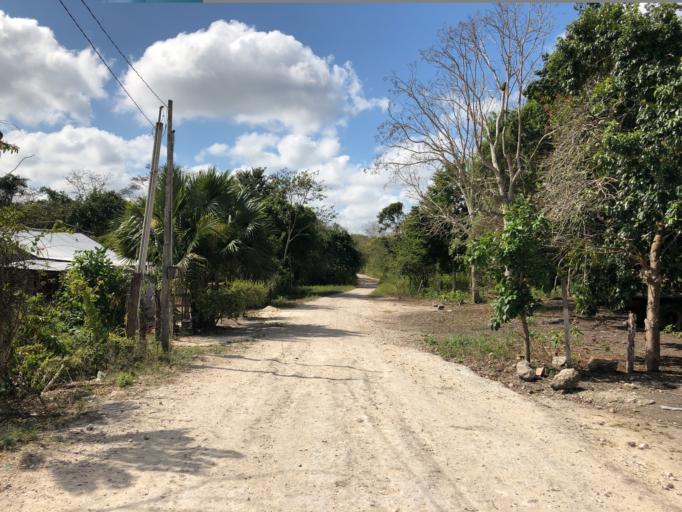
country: MX
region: Quintana Roo
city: Nicolas Bravo
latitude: 18.4465
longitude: -89.3072
